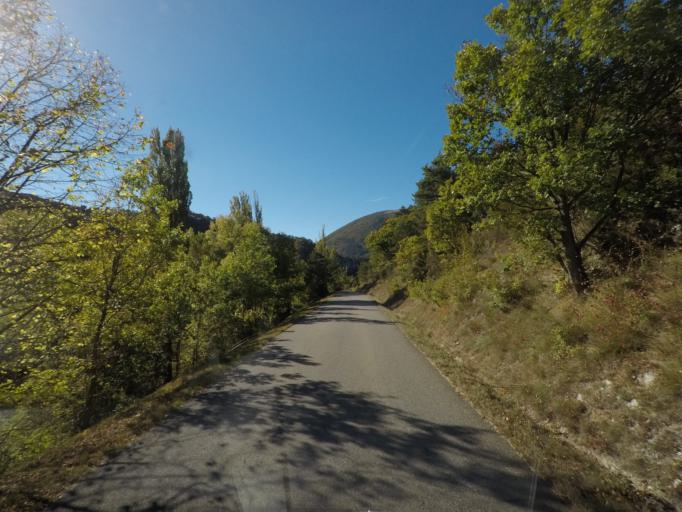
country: FR
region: Provence-Alpes-Cote d'Azur
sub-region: Departement des Hautes-Alpes
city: Serres
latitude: 44.4700
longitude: 5.4653
